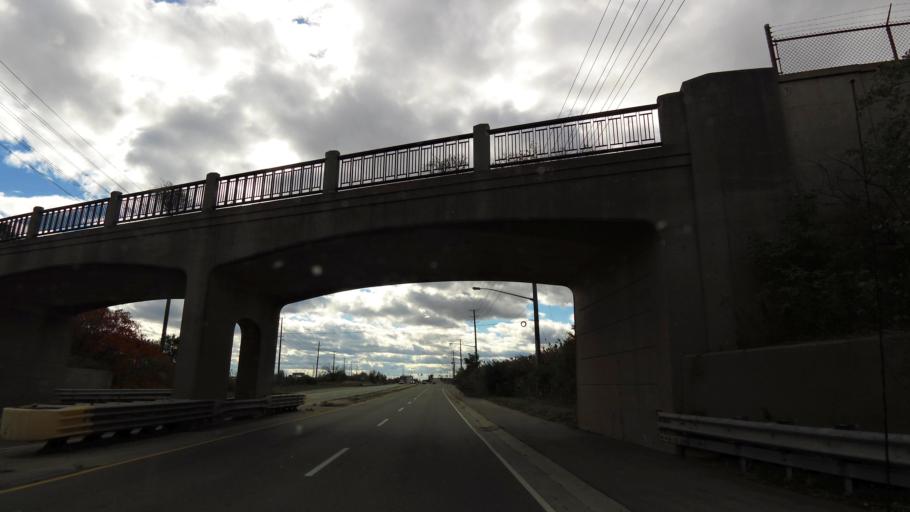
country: CA
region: Ontario
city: Oakville
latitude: 43.4777
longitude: -79.6663
